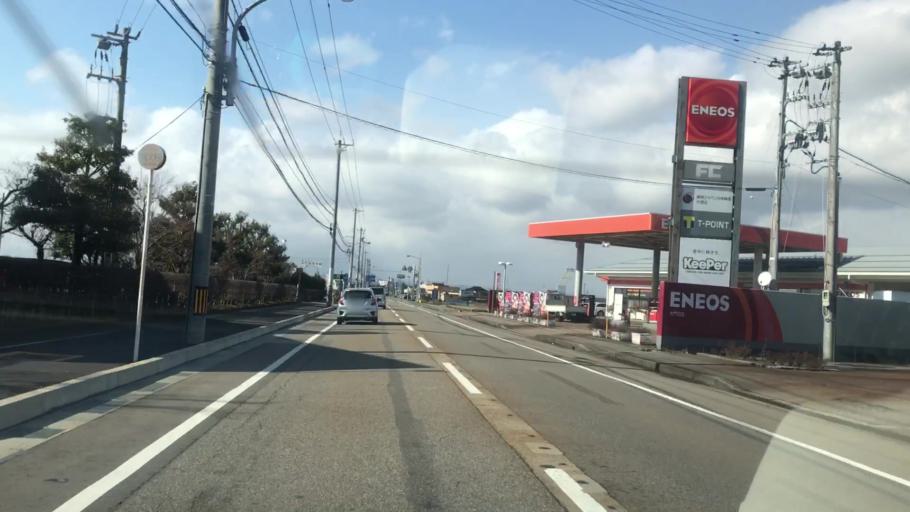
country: JP
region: Toyama
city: Takaoka
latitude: 36.7259
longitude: 137.0642
